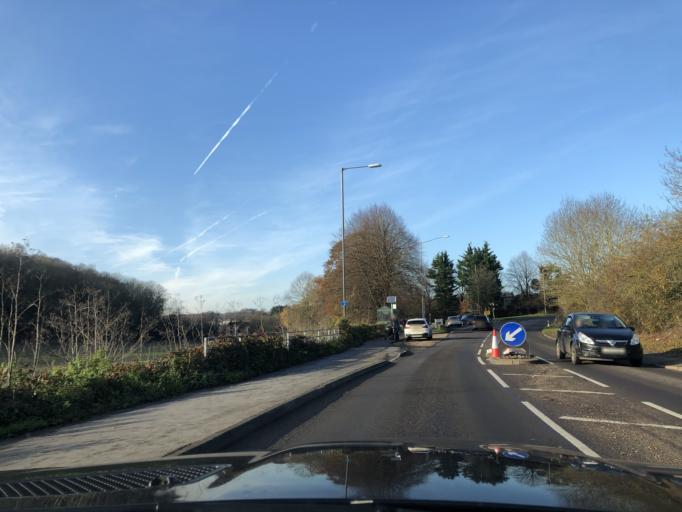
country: GB
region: England
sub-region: Buckinghamshire
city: Marlow
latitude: 51.5852
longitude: -0.7662
